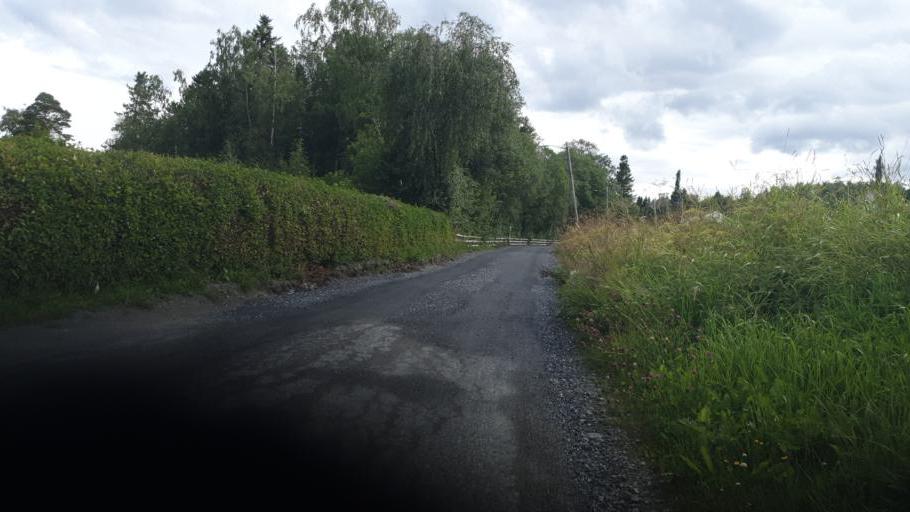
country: NO
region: Sor-Trondelag
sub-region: Malvik
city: Malvik
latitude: 63.4338
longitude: 10.6888
